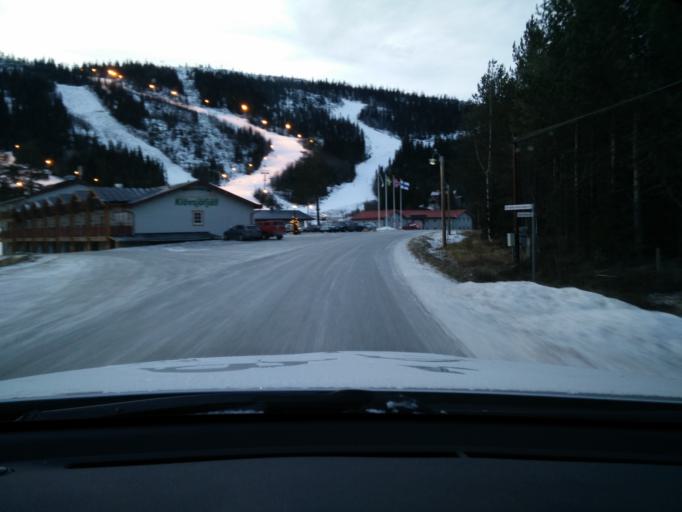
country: SE
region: Jaemtland
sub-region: Bergs Kommun
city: Hoverberg
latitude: 62.5033
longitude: 14.1820
